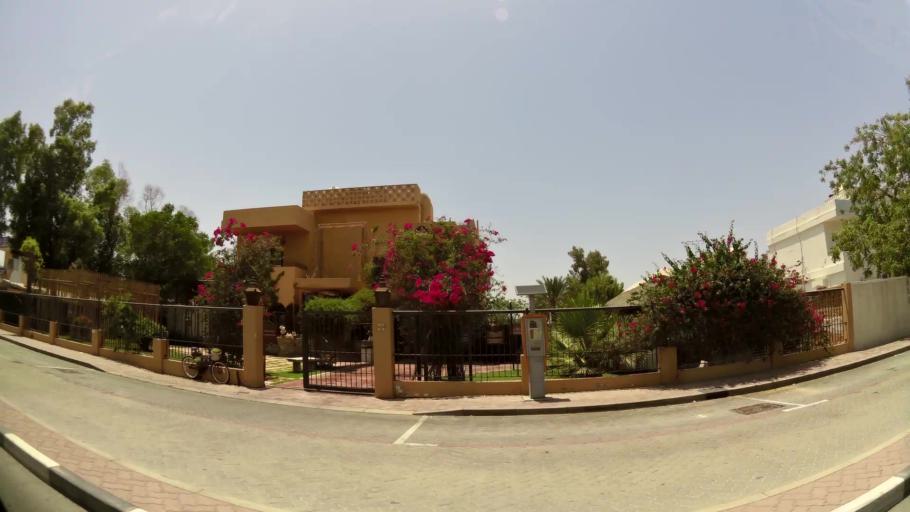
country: AE
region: Dubai
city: Dubai
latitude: 25.2133
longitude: 55.2579
